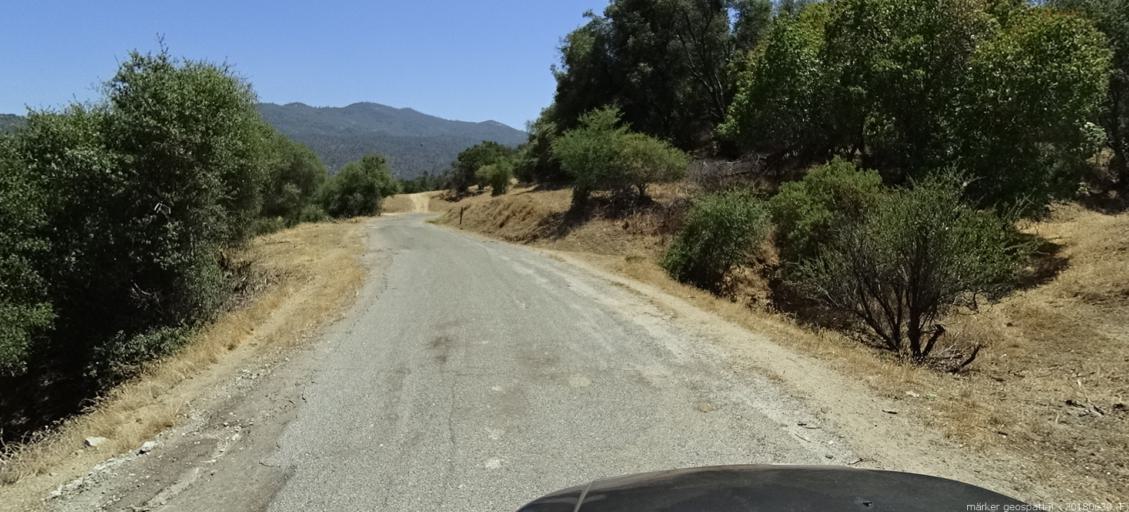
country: US
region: California
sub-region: Fresno County
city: Auberry
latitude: 37.1636
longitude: -119.4405
